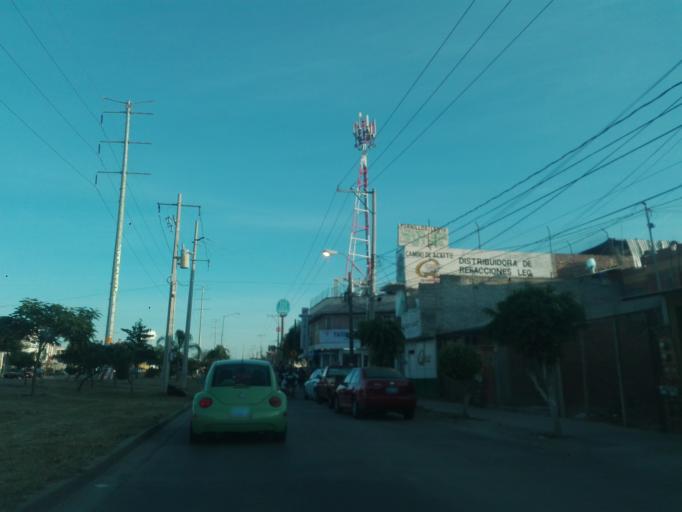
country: MX
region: Guanajuato
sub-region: Leon
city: Fraccionamiento Paraiso Real
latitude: 21.0793
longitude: -101.6214
